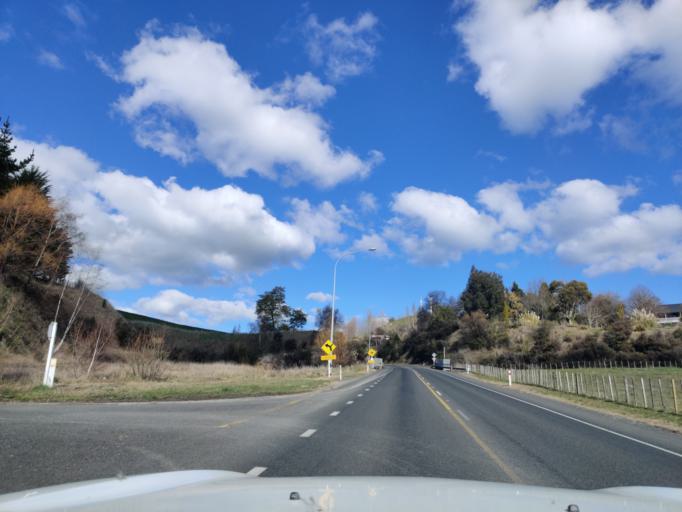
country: NZ
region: Manawatu-Wanganui
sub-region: Ruapehu District
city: Waiouru
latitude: -39.6829
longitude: 175.8009
